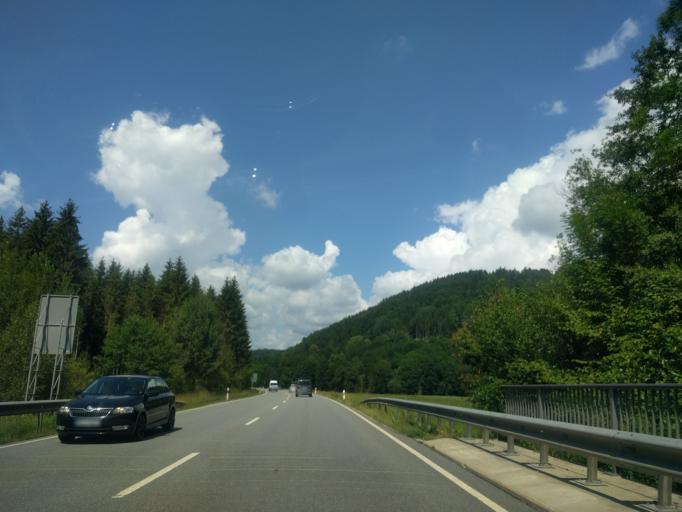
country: DE
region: Bavaria
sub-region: Lower Bavaria
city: Innernzell
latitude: 48.8391
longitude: 13.3140
